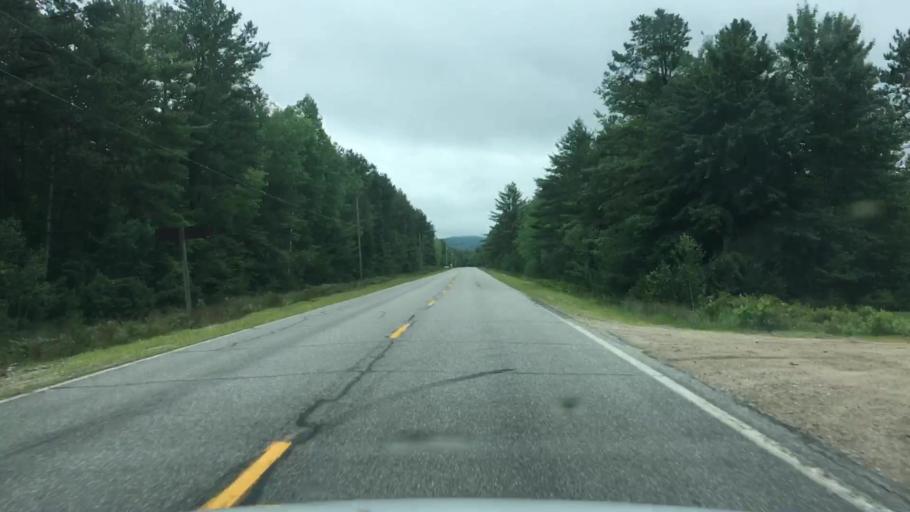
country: US
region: Maine
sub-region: Oxford County
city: Brownfield
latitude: 43.9406
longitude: -70.8867
